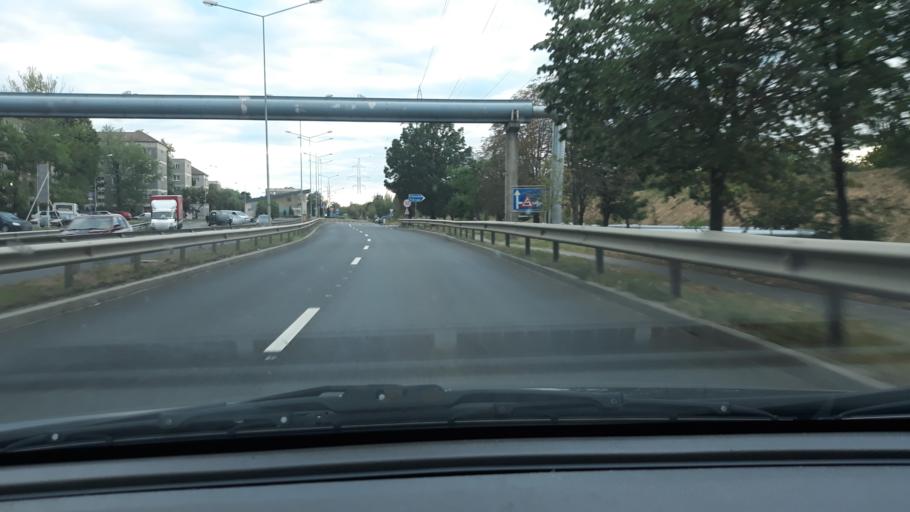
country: RO
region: Bihor
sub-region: Comuna Biharea
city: Oradea
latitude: 47.0810
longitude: 21.9123
